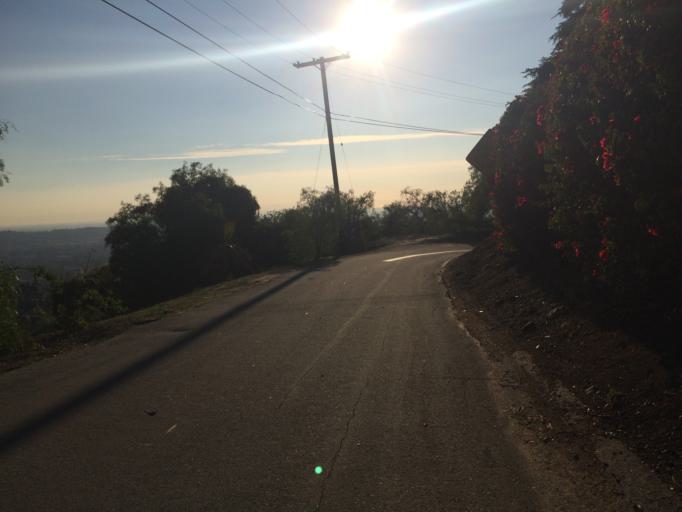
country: US
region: California
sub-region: Los Angeles County
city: La Habra Heights
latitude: 33.9545
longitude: -117.9476
